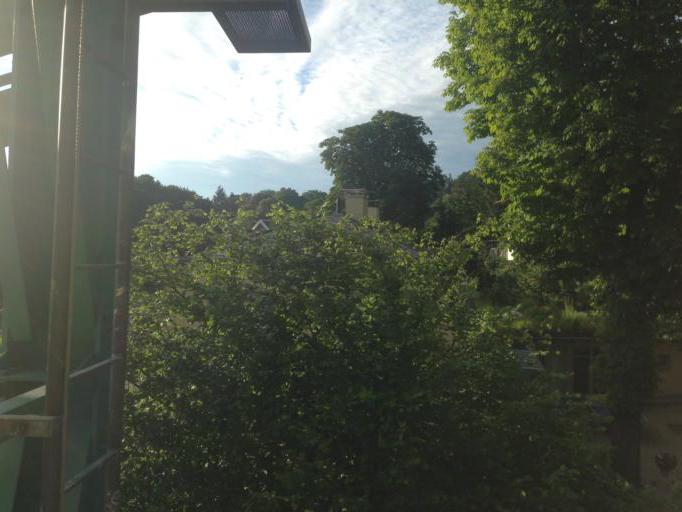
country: DE
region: Saxony
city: Albertstadt
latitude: 51.0539
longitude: 13.8176
